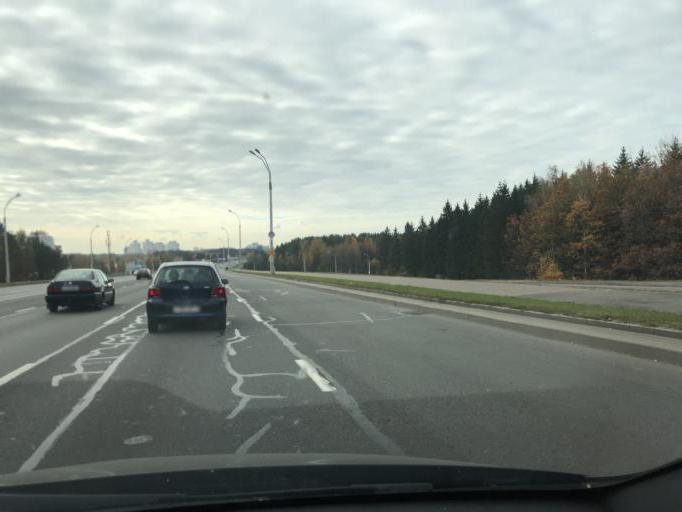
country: BY
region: Minsk
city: Lyeskawka
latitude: 53.9593
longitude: 27.7283
